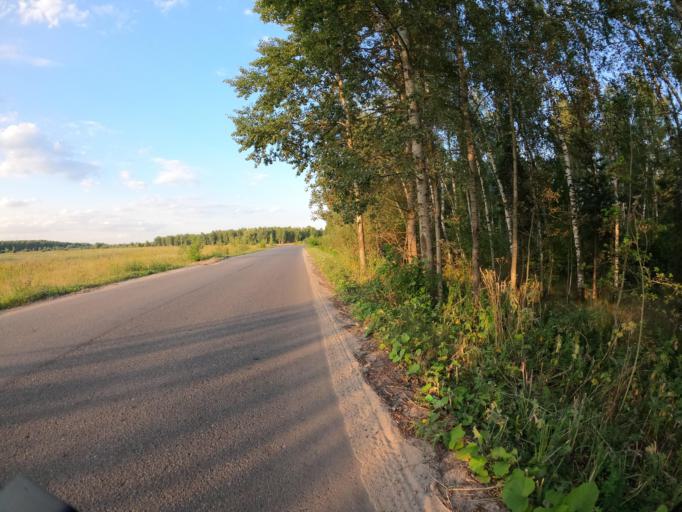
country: RU
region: Moskovskaya
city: Malyshevo
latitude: 55.5187
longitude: 38.2891
